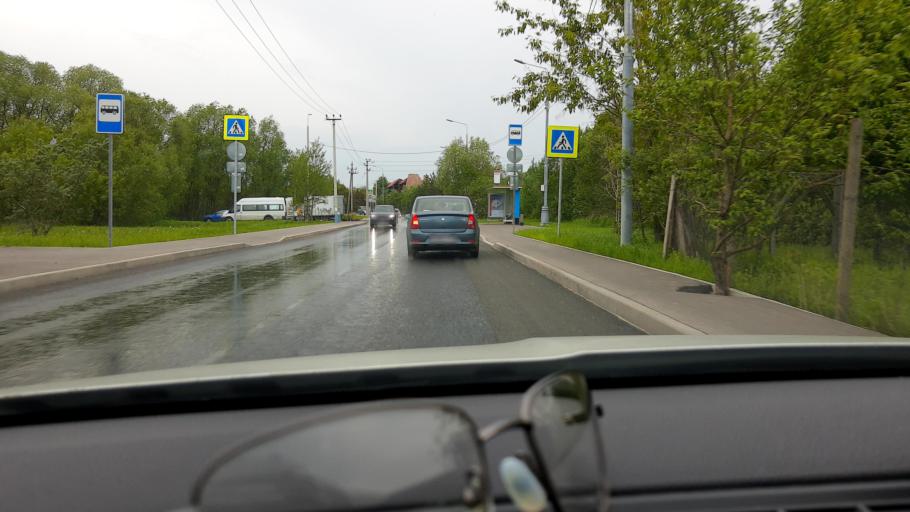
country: RU
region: Moskovskaya
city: Vatutinki
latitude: 55.5204
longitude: 37.3192
